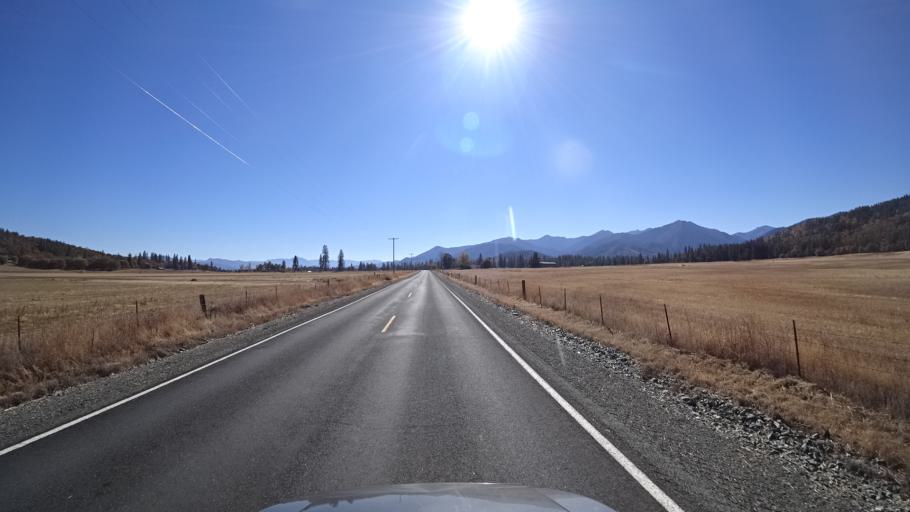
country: US
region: California
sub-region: Siskiyou County
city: Yreka
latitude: 41.5621
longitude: -122.9233
